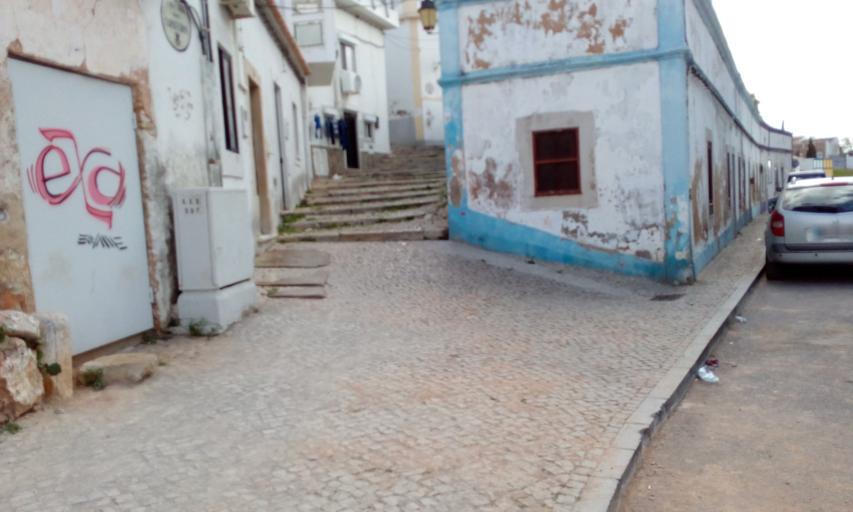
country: PT
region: Faro
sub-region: Loule
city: Loule
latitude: 37.1382
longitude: -8.0242
